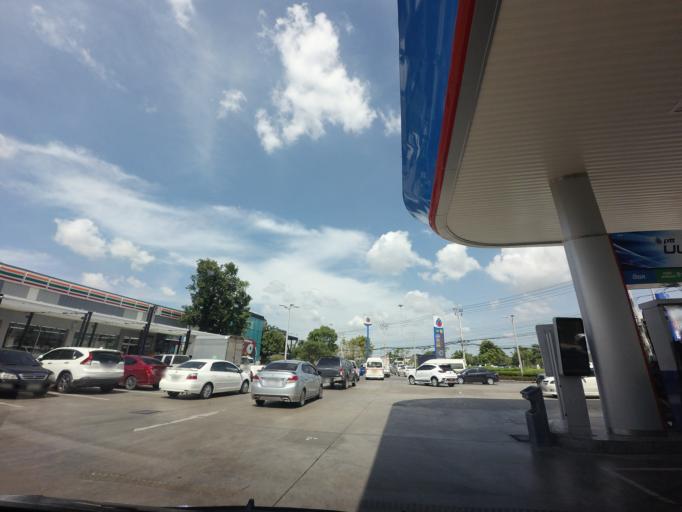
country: TH
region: Bangkok
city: Bang Bon
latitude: 13.6251
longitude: 100.3934
